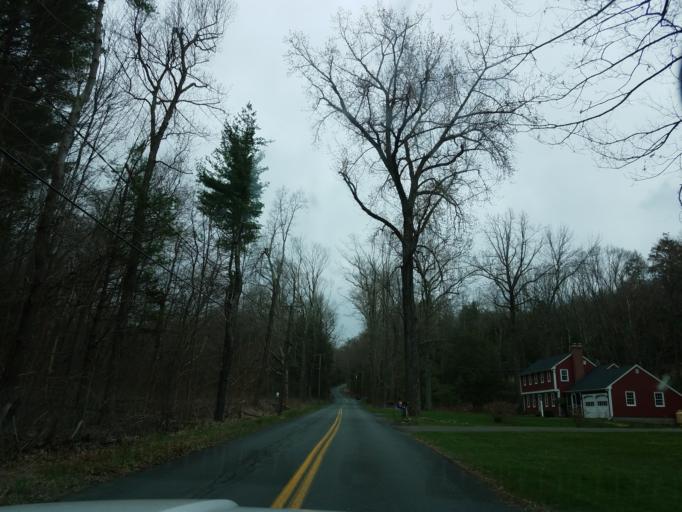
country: US
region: Connecticut
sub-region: Tolland County
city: Somers
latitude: 41.9806
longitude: -72.4219
